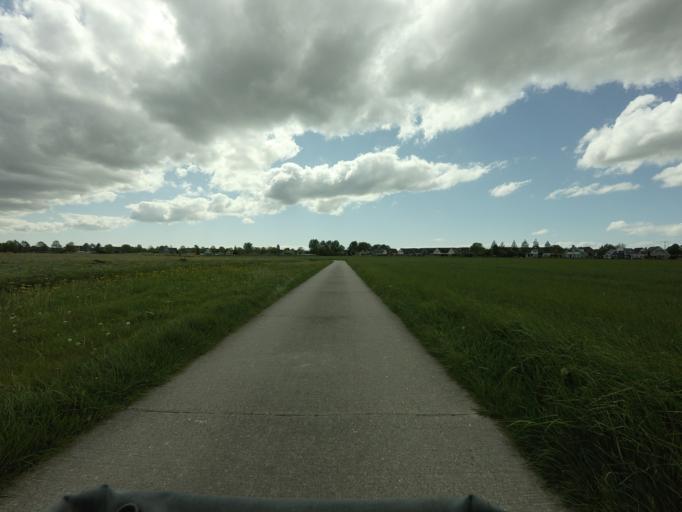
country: NL
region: Friesland
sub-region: Sudwest Fryslan
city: Bolsward
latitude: 53.0724
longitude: 5.5418
